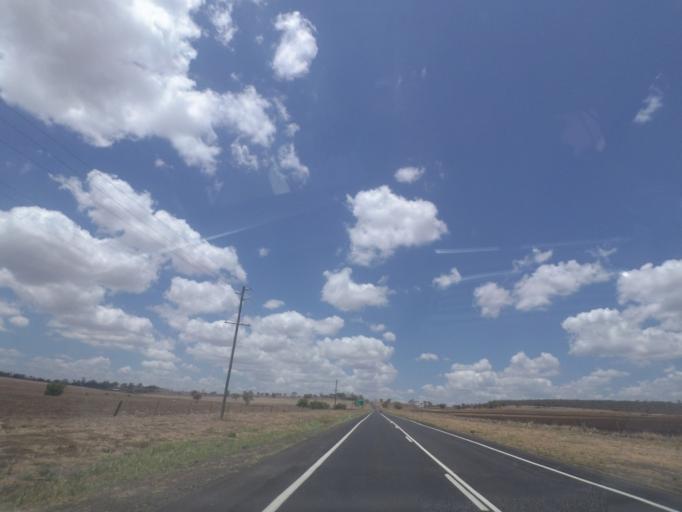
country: AU
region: Queensland
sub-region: Toowoomba
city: Top Camp
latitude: -27.7203
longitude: 151.9116
